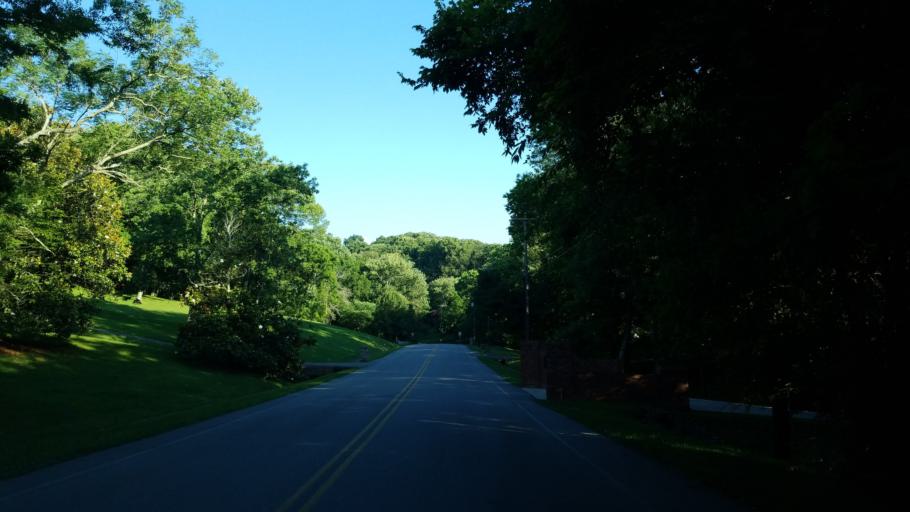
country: US
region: Tennessee
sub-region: Williamson County
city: Brentwood
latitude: 36.0487
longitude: -86.7908
